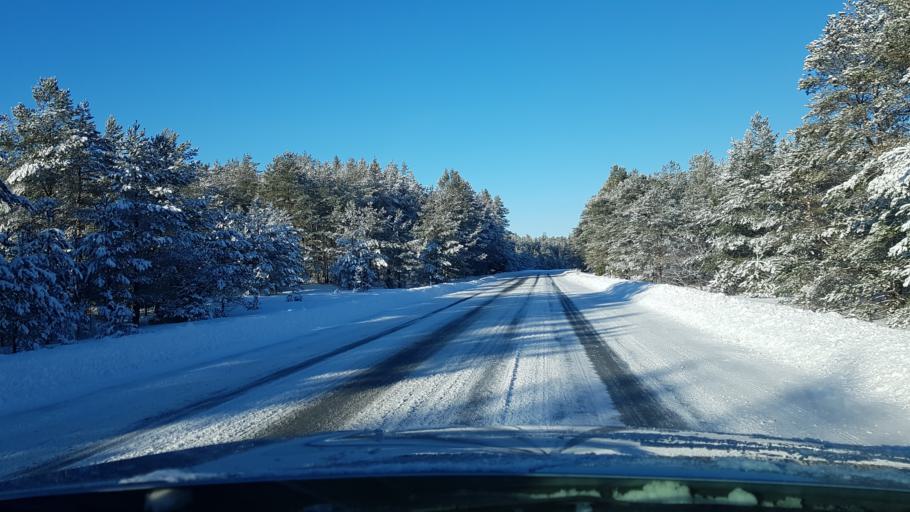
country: EE
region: Hiiumaa
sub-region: Kaerdla linn
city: Kardla
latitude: 58.9448
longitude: 22.7734
